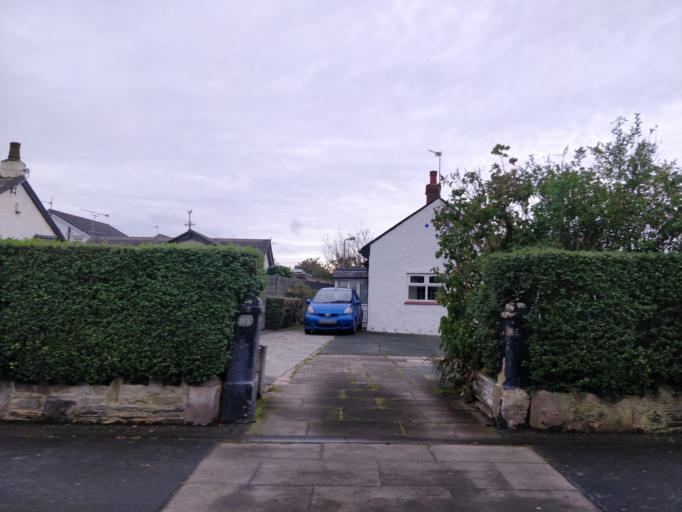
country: GB
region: England
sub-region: Sefton
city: Southport
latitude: 53.6673
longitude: -2.9704
